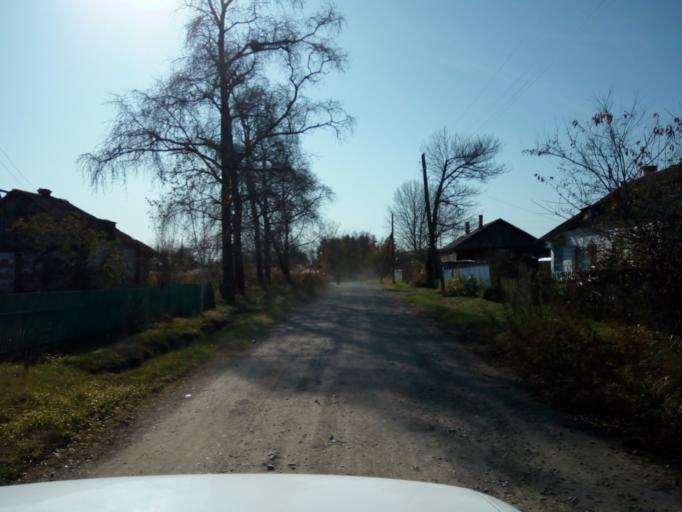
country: RU
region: Primorskiy
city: Dal'nerechensk
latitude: 45.9133
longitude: 133.8017
